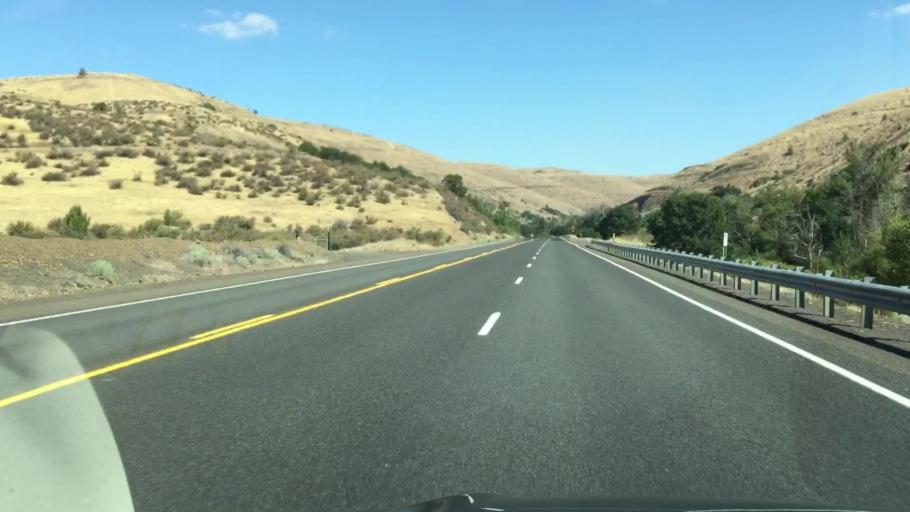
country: US
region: Oregon
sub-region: Wasco County
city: The Dalles
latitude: 45.2653
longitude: -121.1905
